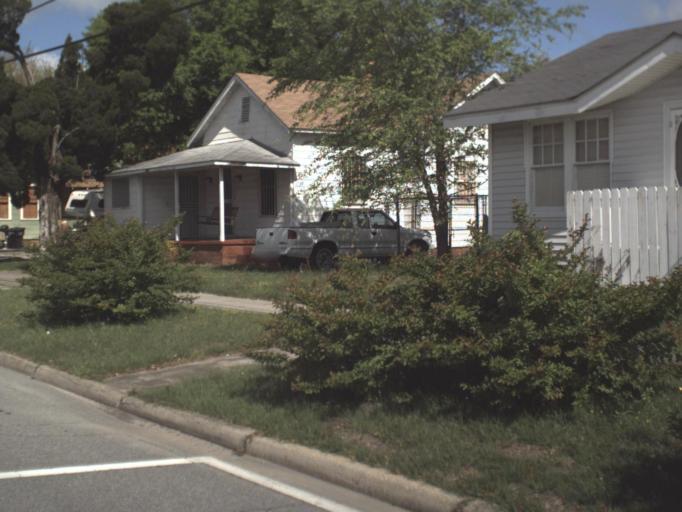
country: US
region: Florida
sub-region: Escambia County
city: Pensacola
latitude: 30.4115
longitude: -87.2329
